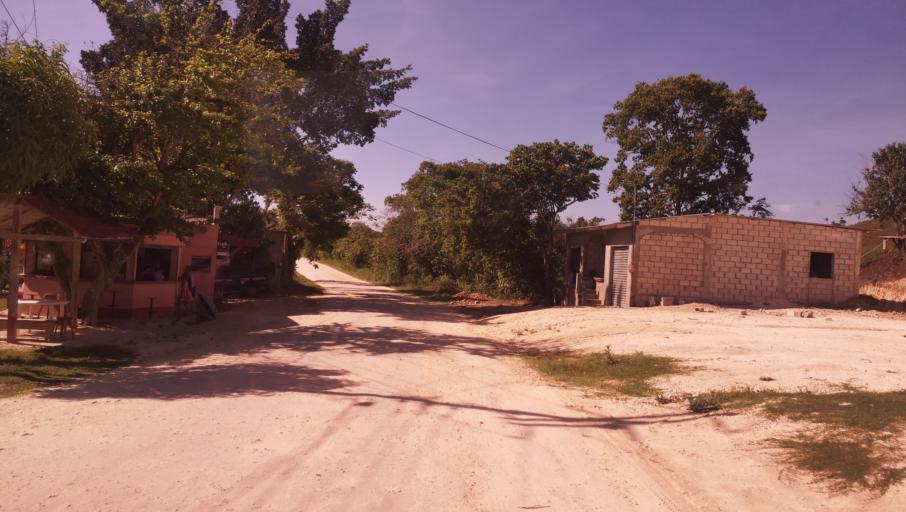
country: GT
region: Peten
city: Dolores
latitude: 16.7234
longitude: -89.3783
